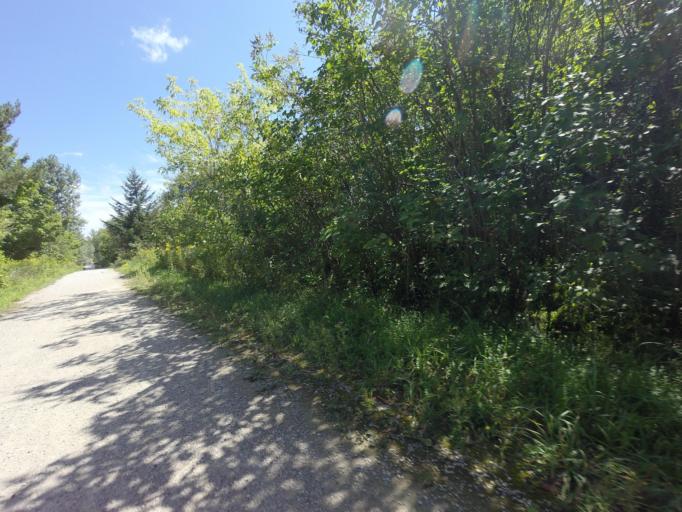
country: CA
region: Ontario
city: Orangeville
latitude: 43.7849
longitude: -80.1405
